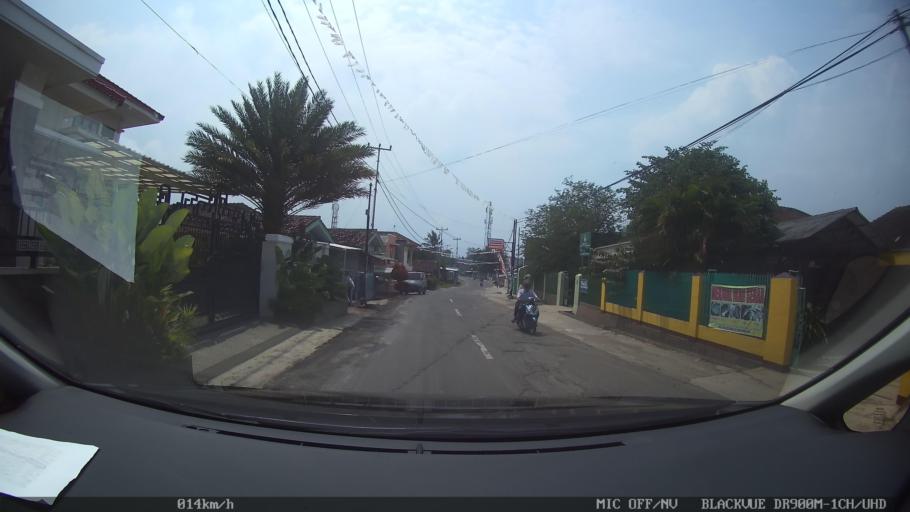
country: ID
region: Lampung
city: Bandarlampung
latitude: -5.4347
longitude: 105.2681
